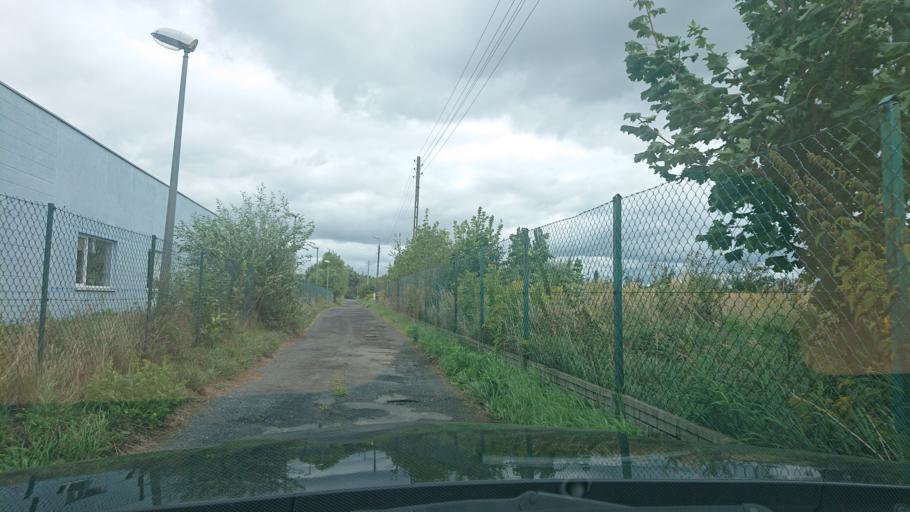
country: PL
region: Greater Poland Voivodeship
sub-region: Powiat gnieznienski
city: Gniezno
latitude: 52.5243
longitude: 17.6169
